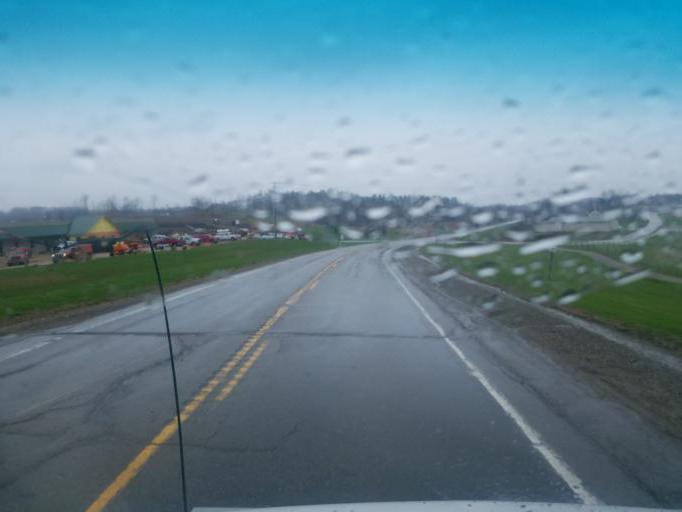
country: US
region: Ohio
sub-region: Holmes County
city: Millersburg
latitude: 40.6205
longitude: -81.9205
